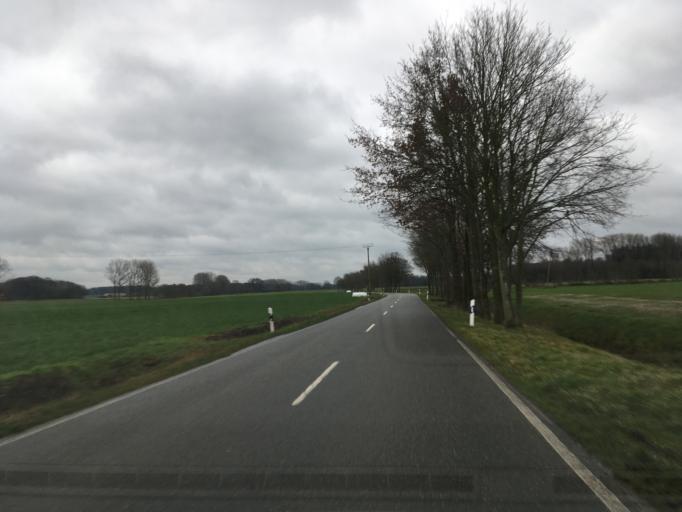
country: DE
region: North Rhine-Westphalia
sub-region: Regierungsbezirk Munster
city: Legden
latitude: 52.0502
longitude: 7.1480
